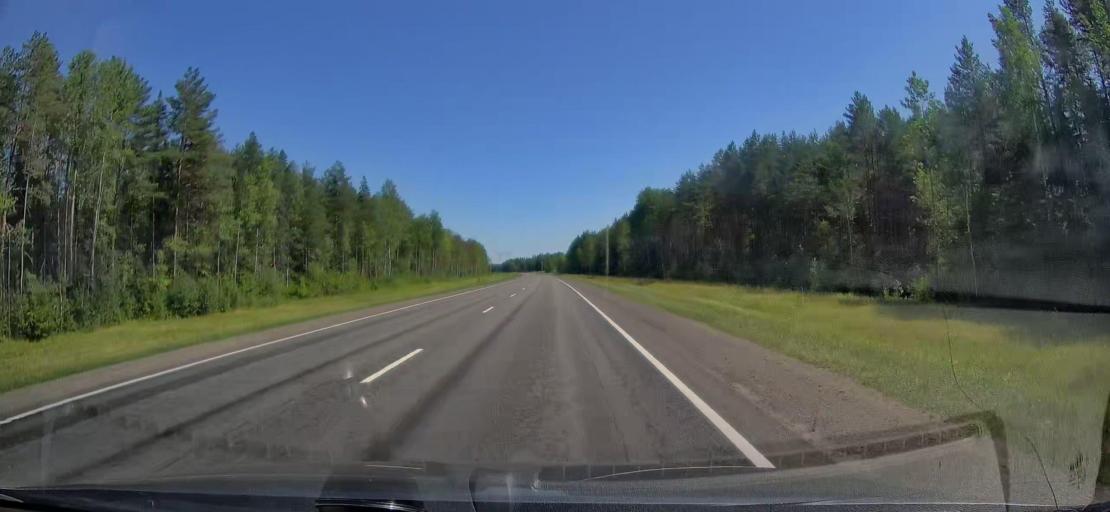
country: RU
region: Tverskaya
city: Ves'yegonsk
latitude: 58.9215
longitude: 37.2084
